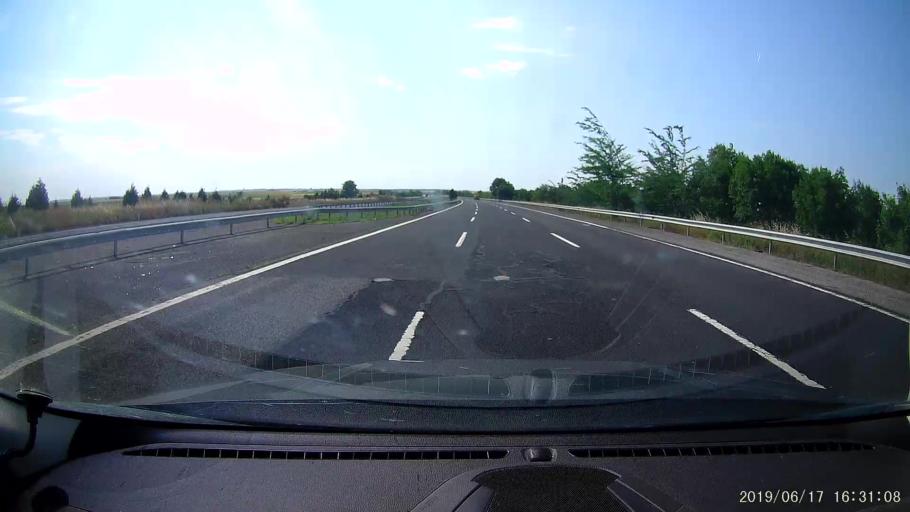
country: TR
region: Tekirdag
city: Beyazkoy
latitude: 41.3582
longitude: 27.6373
